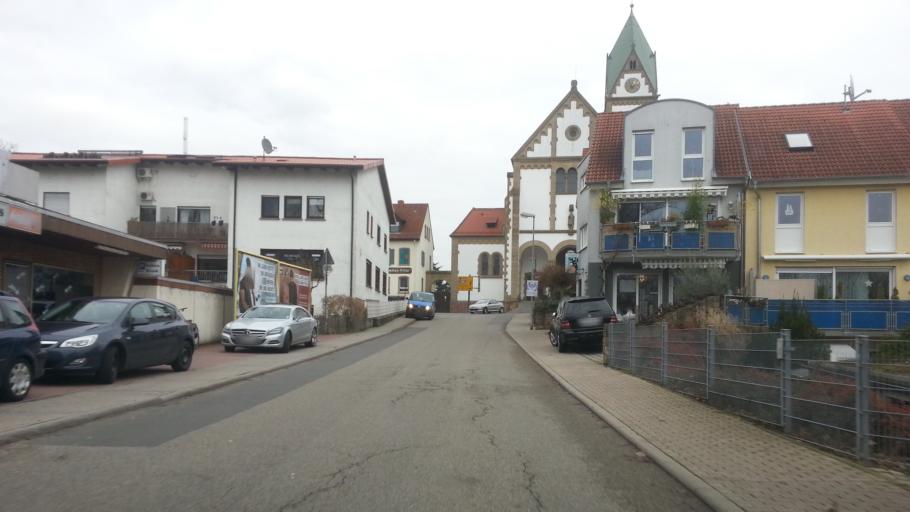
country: DE
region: Baden-Wuerttemberg
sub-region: Karlsruhe Region
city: Ketsch
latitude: 49.3674
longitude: 8.5226
